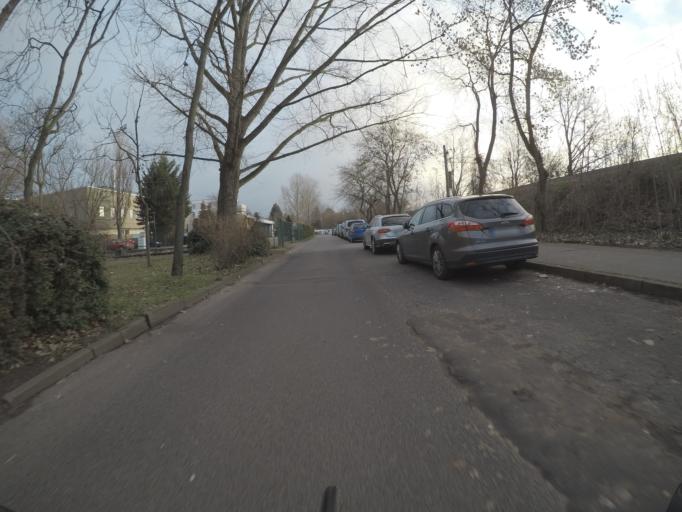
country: DE
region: Berlin
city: Friedrichsfelde
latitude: 52.4928
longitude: 13.5178
